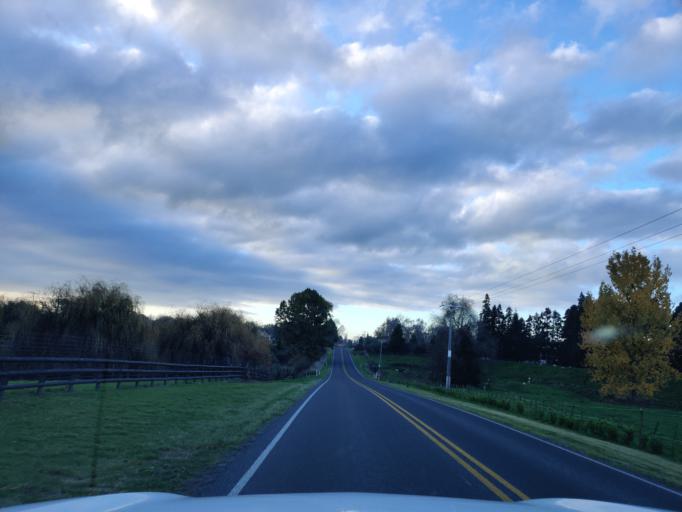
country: NZ
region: Waikato
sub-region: Waipa District
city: Cambridge
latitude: -37.8541
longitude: 175.4390
